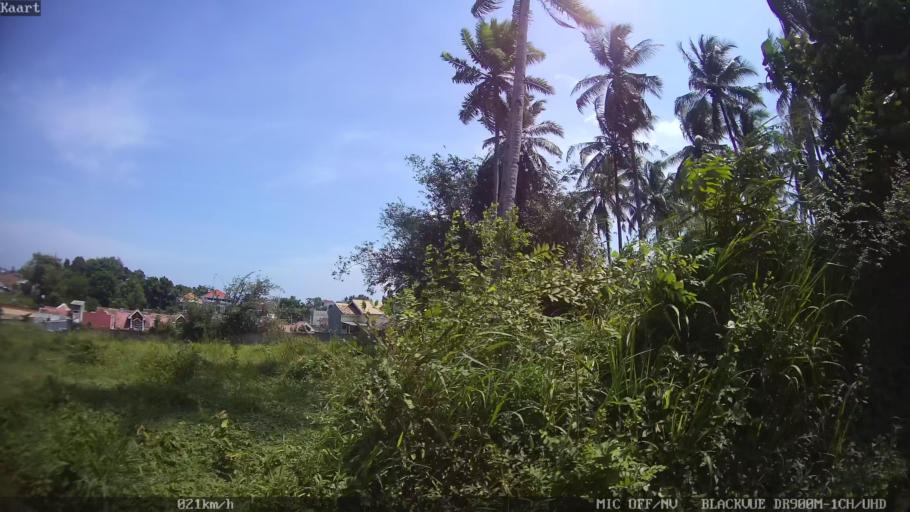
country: ID
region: Lampung
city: Kedaton
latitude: -5.3697
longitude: 105.2576
